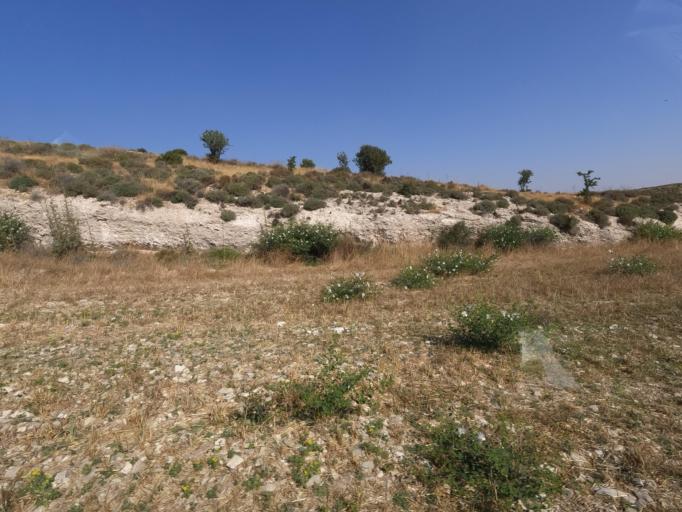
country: CY
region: Lefkosia
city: Lympia
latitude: 34.9806
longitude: 33.4801
